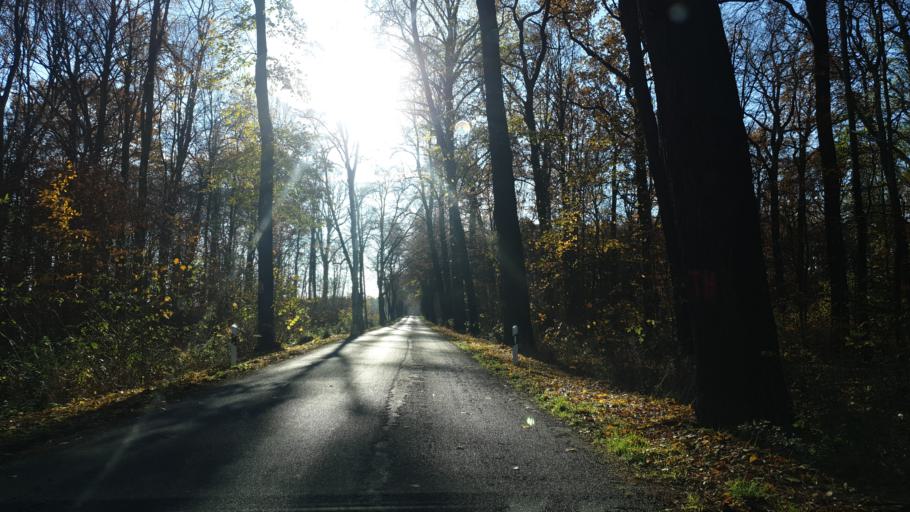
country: DE
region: Saxony-Anhalt
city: Droyssig
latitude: 51.0309
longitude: 12.0215
